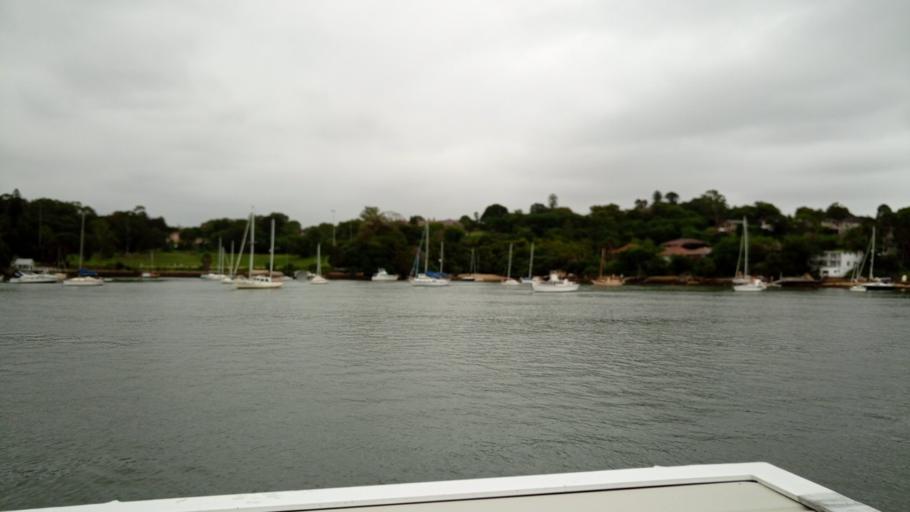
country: AU
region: New South Wales
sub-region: Hunters Hill
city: Gladesville
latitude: -33.8434
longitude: 151.1307
